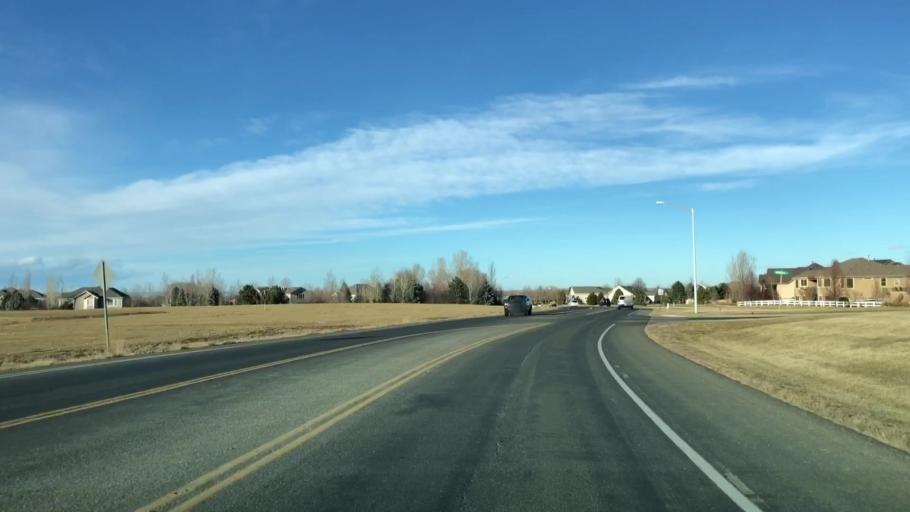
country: US
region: Colorado
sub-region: Weld County
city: Windsor
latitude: 40.4659
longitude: -104.9827
